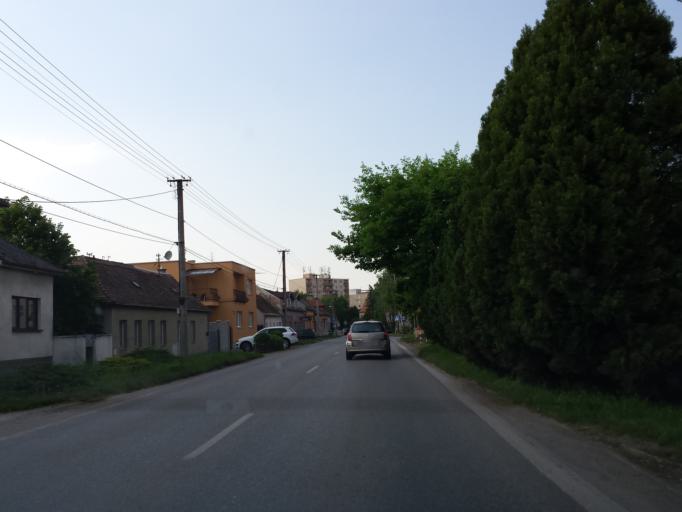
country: SK
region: Bratislavsky
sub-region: Okres Malacky
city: Malacky
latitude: 48.4323
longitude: 17.0188
